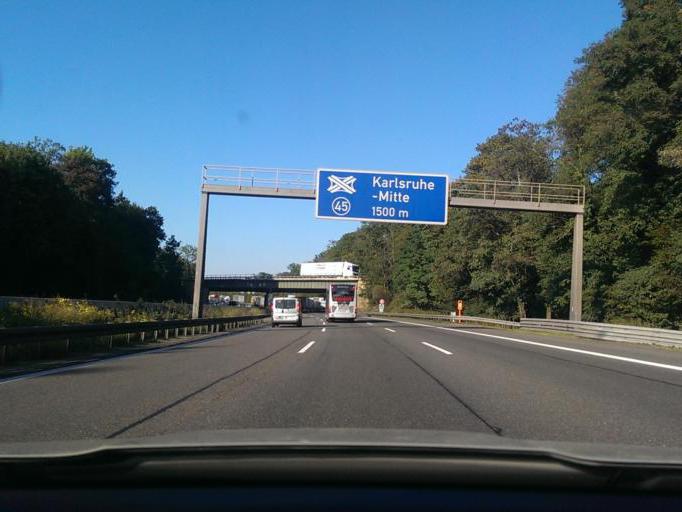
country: DE
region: Baden-Wuerttemberg
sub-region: Karlsruhe Region
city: Ettlingen
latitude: 48.9731
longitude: 8.4364
